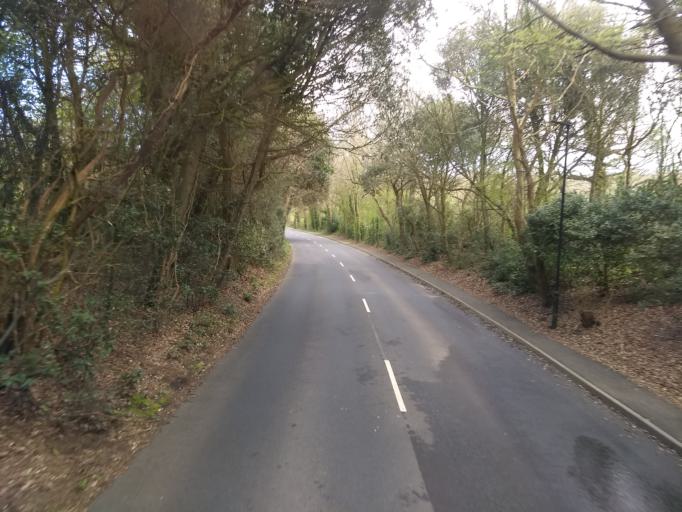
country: GB
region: England
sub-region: Isle of Wight
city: Seaview
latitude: 50.7205
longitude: -1.1349
